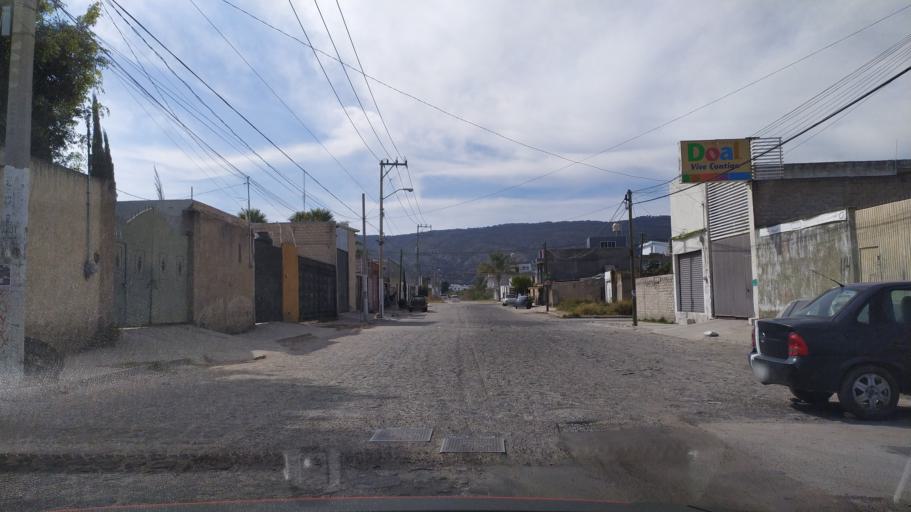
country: MX
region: Jalisco
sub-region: Tlajomulco de Zuniga
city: Palomar
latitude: 20.6285
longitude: -103.4728
